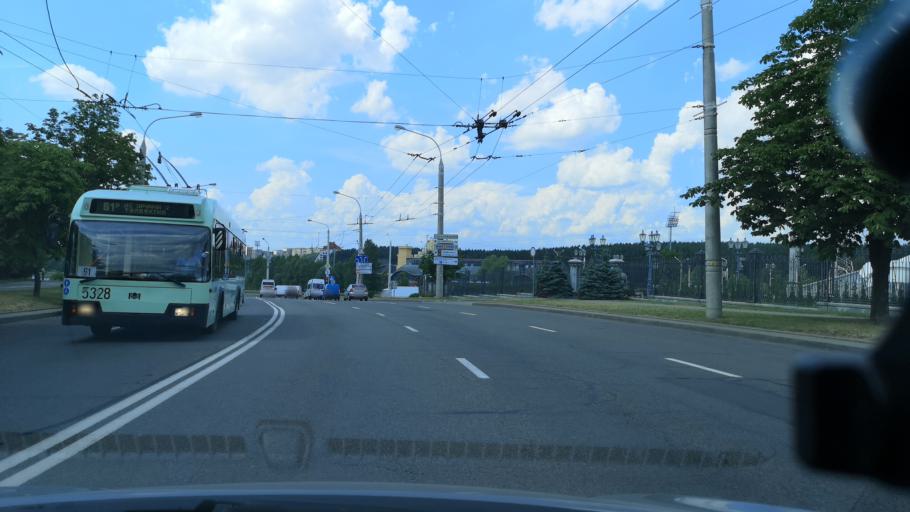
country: BY
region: Minsk
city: Borovlyany
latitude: 53.9413
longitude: 27.6532
